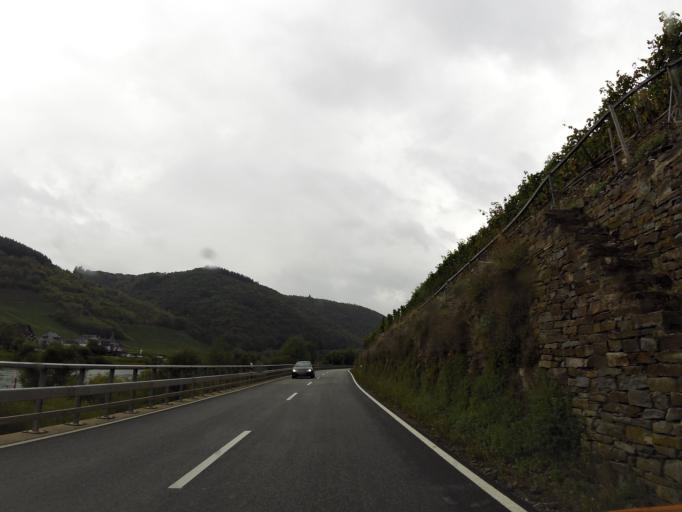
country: DE
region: Rheinland-Pfalz
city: Valwig
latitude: 50.1449
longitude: 7.2185
